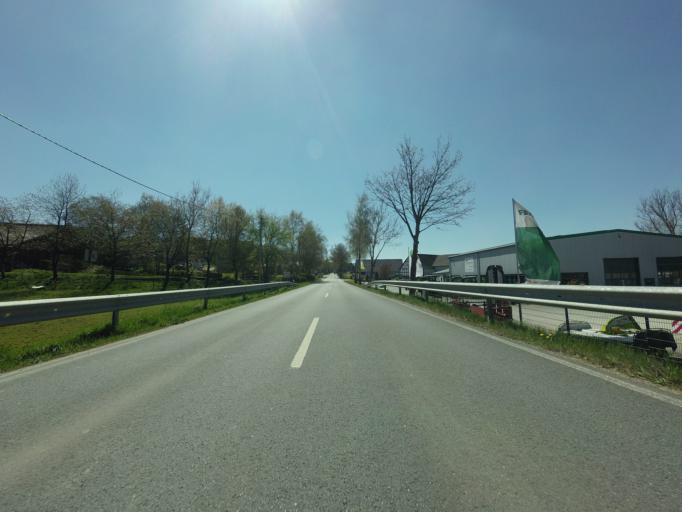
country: DE
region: North Rhine-Westphalia
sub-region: Regierungsbezirk Arnsberg
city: Erndtebruck
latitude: 51.0104
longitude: 8.2603
